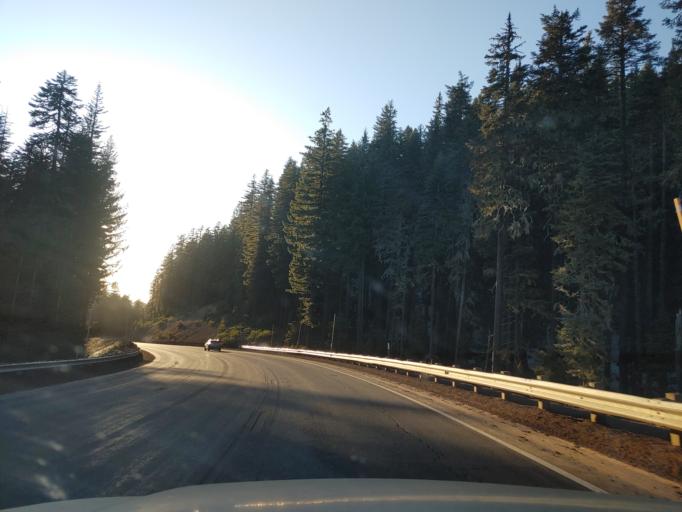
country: US
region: Oregon
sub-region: Lane County
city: Oakridge
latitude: 43.6115
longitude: -122.0603
